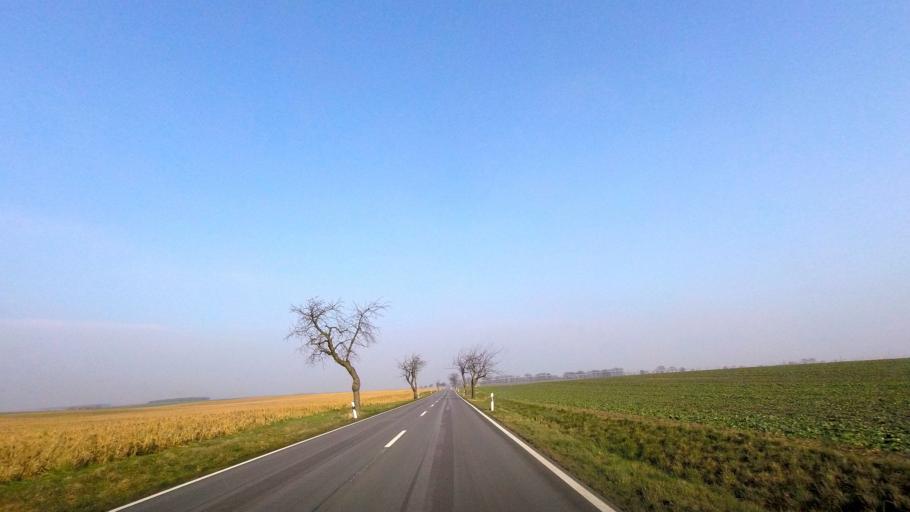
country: DE
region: Brandenburg
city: Niedergorsdorf
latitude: 51.9349
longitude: 13.0355
